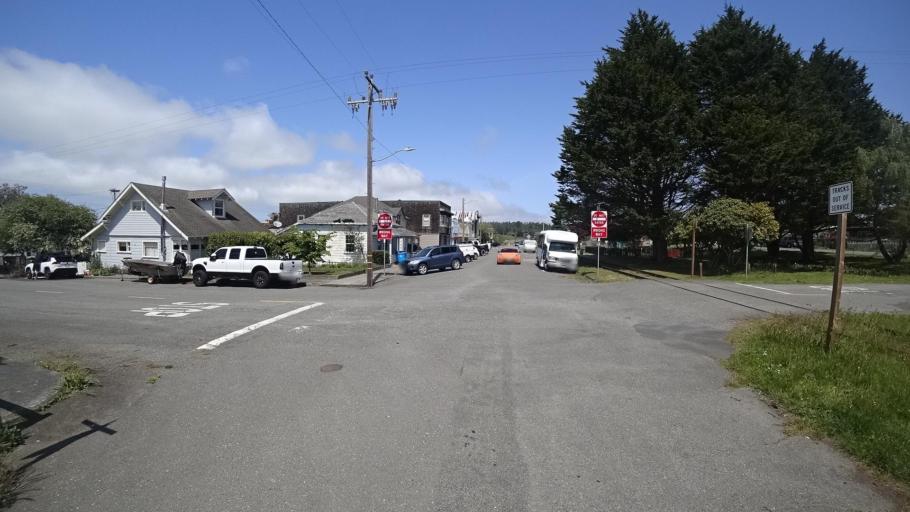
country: US
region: California
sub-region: Humboldt County
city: Ferndale
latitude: 40.6396
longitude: -124.2248
